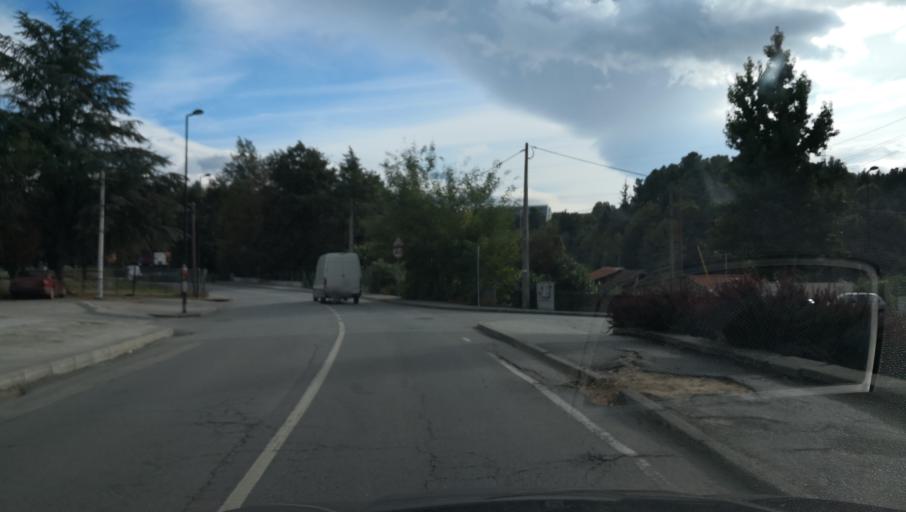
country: PT
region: Vila Real
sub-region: Vila Real
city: Vila Real
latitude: 41.2928
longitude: -7.7375
